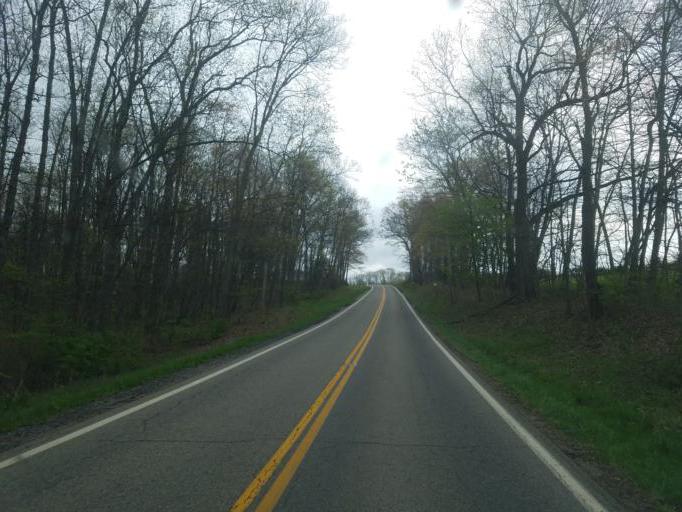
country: US
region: Ohio
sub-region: Ashland County
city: Loudonville
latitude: 40.5676
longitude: -82.1455
